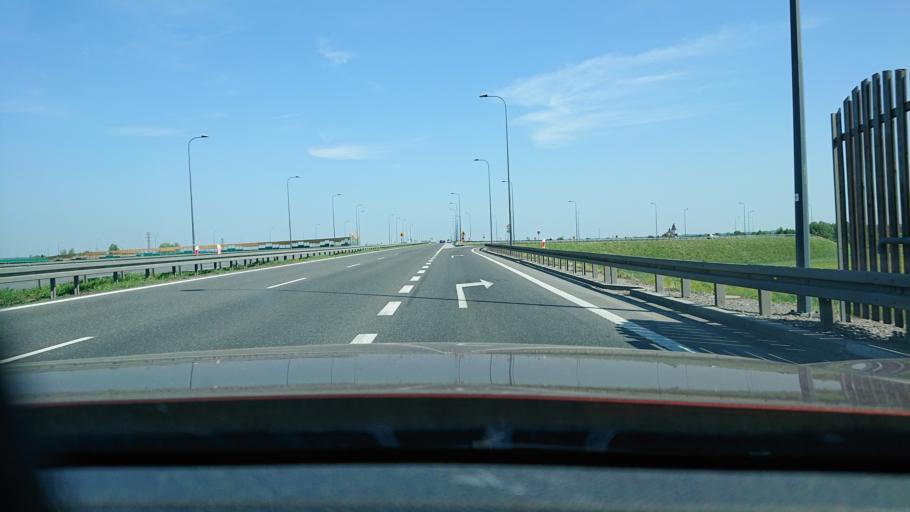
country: PL
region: Subcarpathian Voivodeship
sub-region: Powiat rzeszowski
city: Trzebownisko
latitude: 50.0868
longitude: 22.0614
